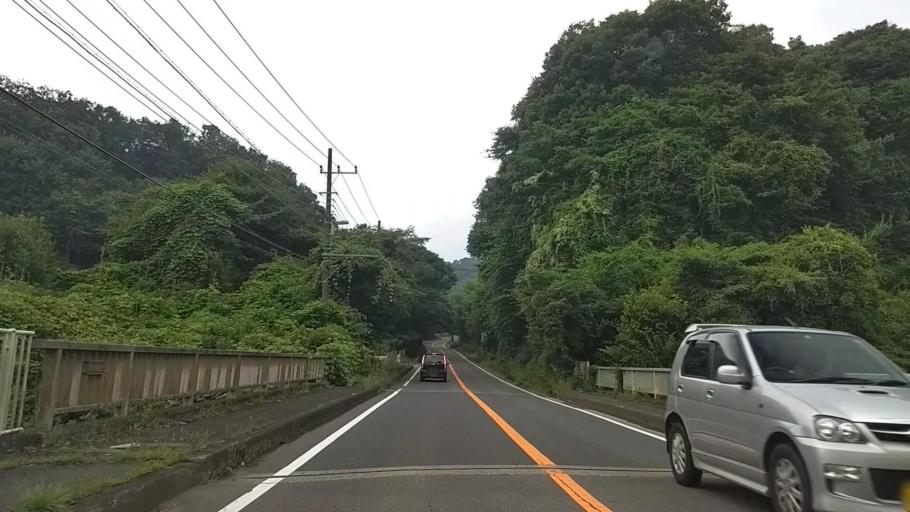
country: JP
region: Kanagawa
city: Hadano
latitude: 35.3412
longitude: 139.1834
